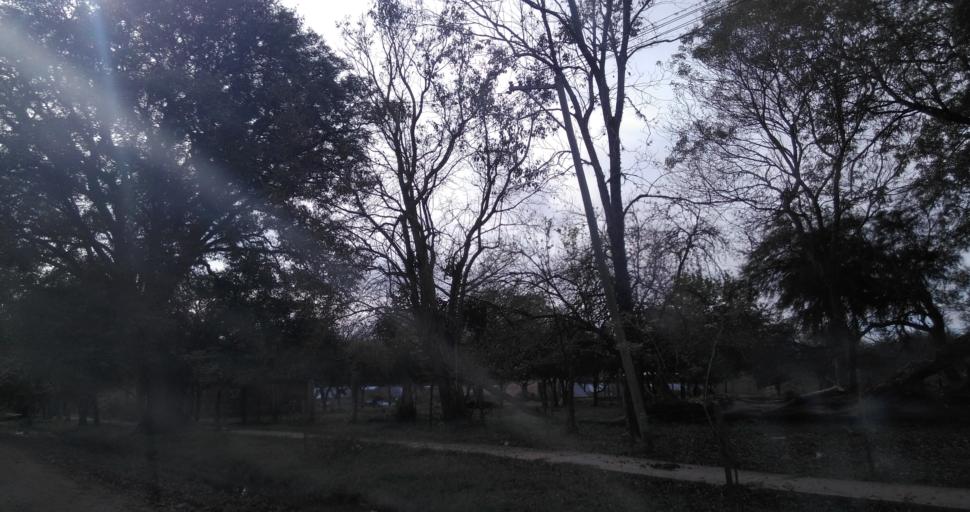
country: AR
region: Chaco
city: Colonia Benitez
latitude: -27.3330
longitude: -58.9541
